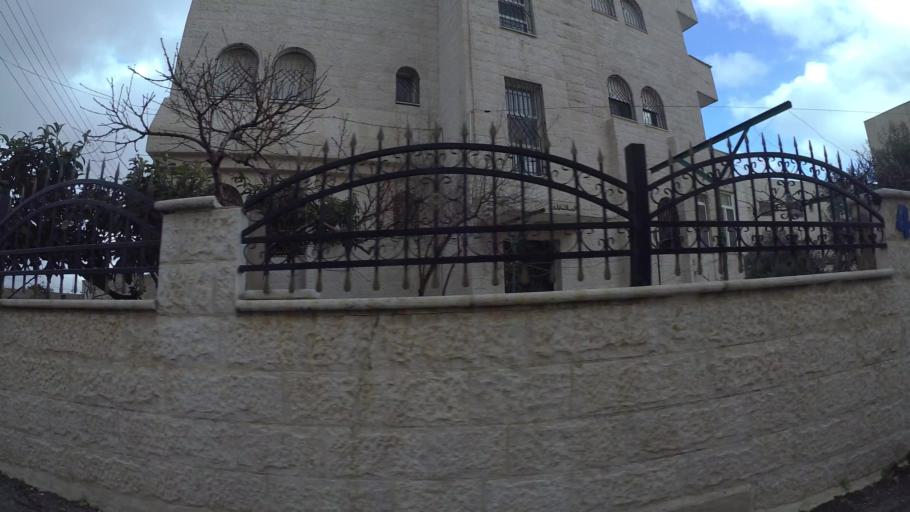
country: JO
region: Amman
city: Al Jubayhah
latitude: 32.0340
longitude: 35.8674
